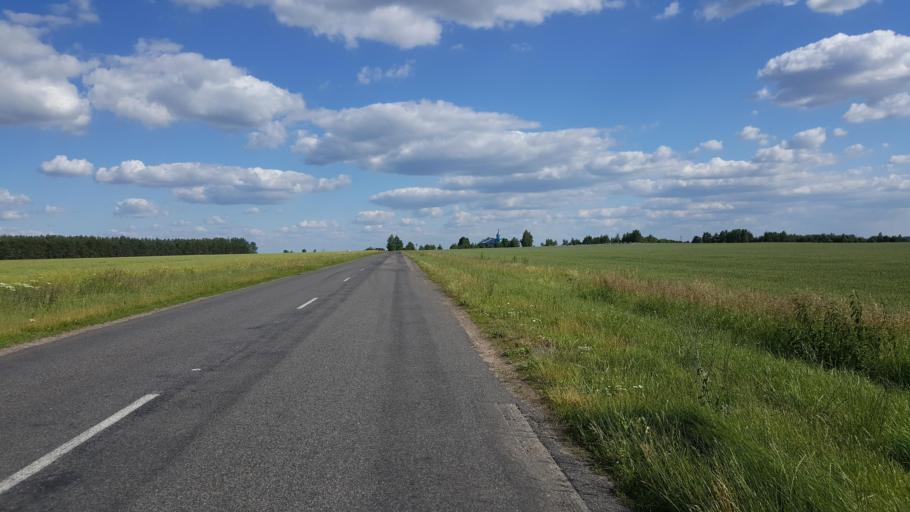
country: BY
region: Brest
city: Kamyanyets
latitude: 52.4508
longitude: 23.7300
